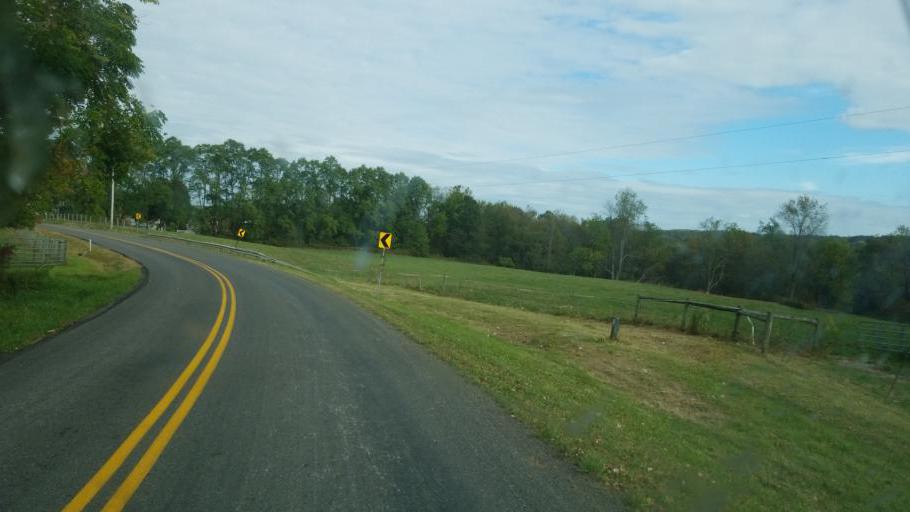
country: US
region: Pennsylvania
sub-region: Mercer County
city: Mercer
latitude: 41.3356
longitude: -80.2615
